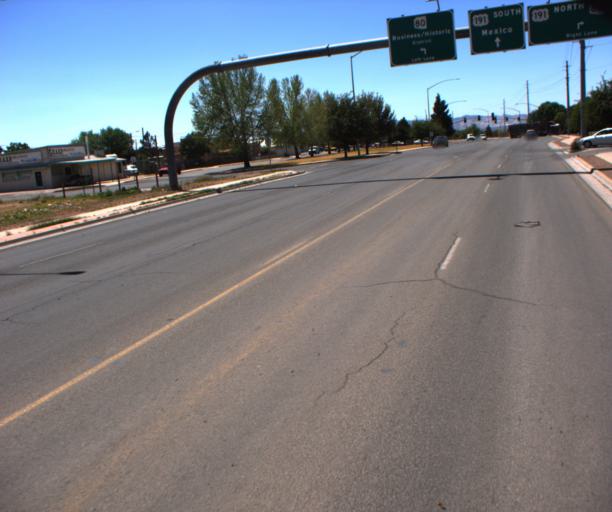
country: US
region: Arizona
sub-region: Cochise County
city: Douglas
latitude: 31.3512
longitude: -109.5538
